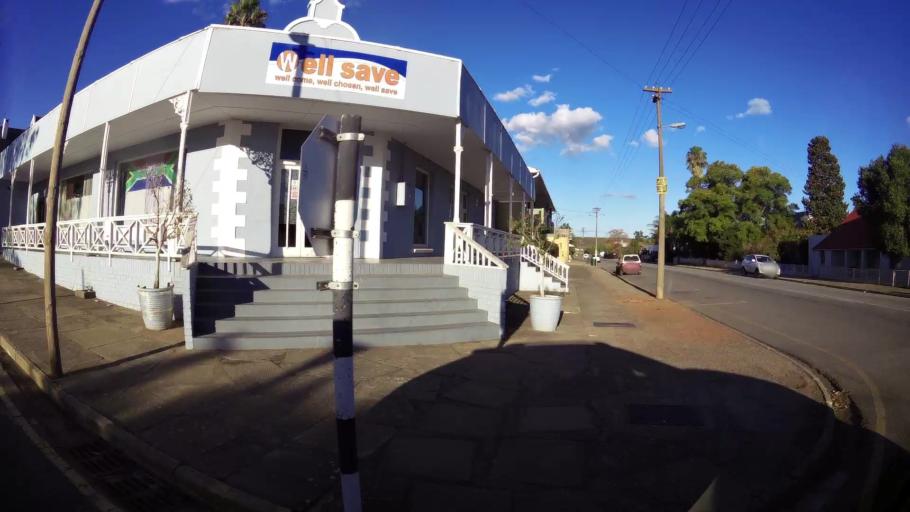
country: ZA
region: Western Cape
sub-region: Eden District Municipality
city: Riversdale
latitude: -34.0902
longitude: 20.9588
